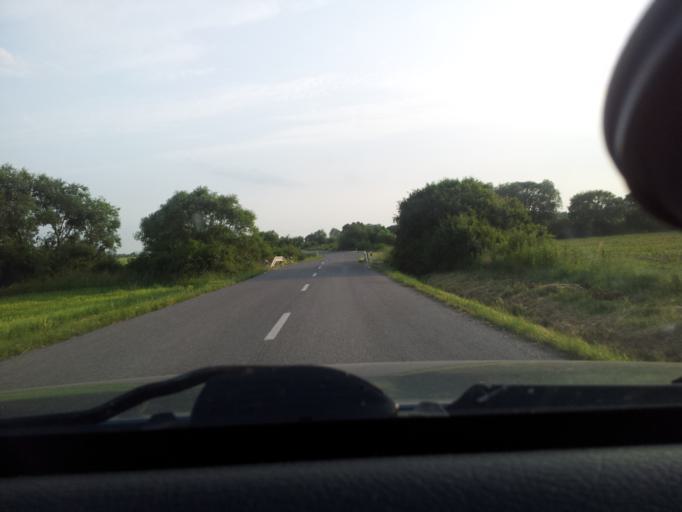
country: SK
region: Nitriansky
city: Levice
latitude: 48.3085
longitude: 18.6854
